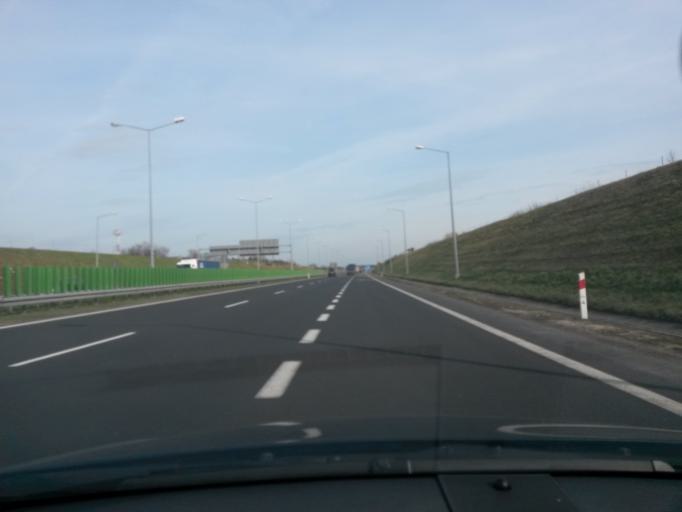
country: PL
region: Greater Poland Voivodeship
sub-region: Powiat poznanski
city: Daszewice
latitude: 52.3446
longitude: 17.0116
